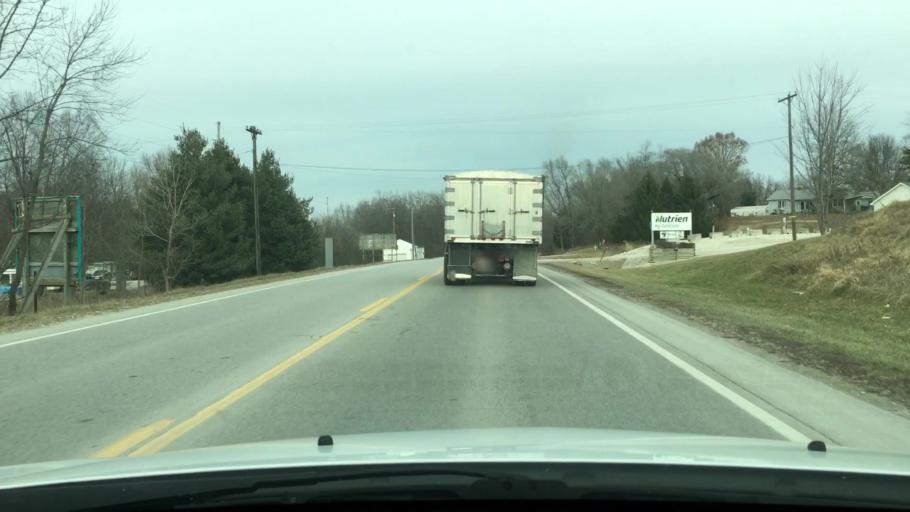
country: US
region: Illinois
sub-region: Pike County
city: Pittsfield
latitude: 39.6208
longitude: -90.8008
